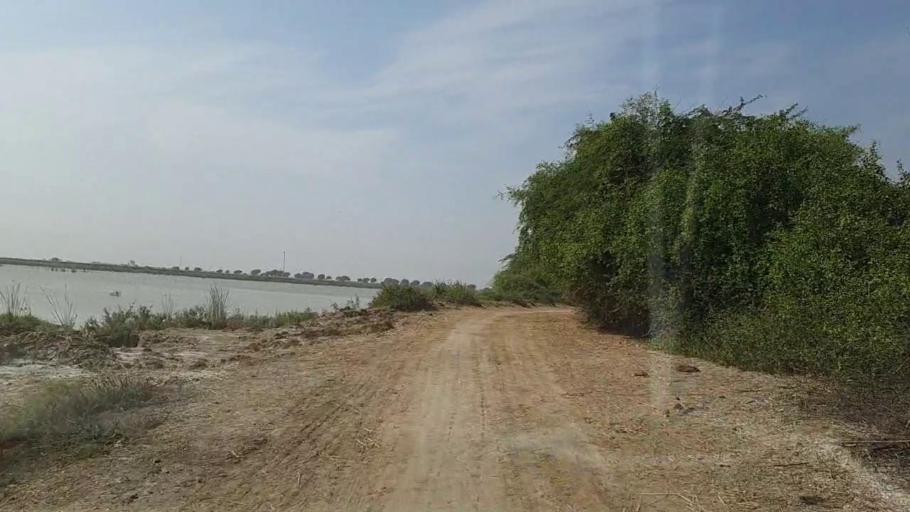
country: PK
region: Sindh
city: Mirpur Batoro
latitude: 24.6087
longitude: 68.2120
